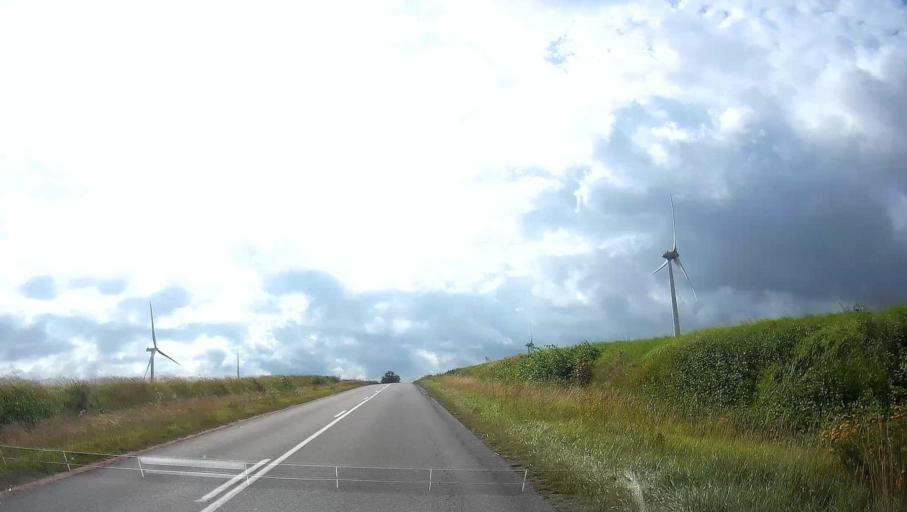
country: FR
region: Champagne-Ardenne
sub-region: Departement des Ardennes
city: Rethel
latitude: 49.5366
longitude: 4.3192
